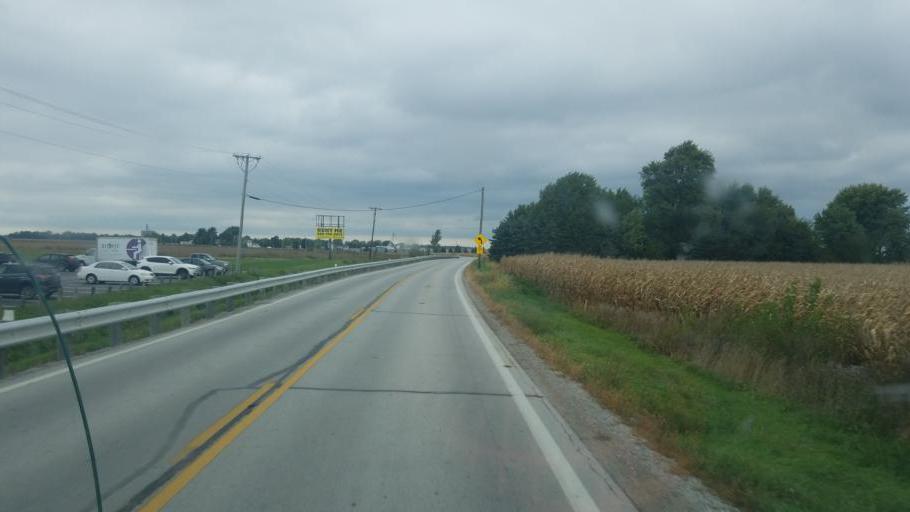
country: US
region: Ohio
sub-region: Wood County
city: Haskins
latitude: 41.4472
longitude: -83.6972
